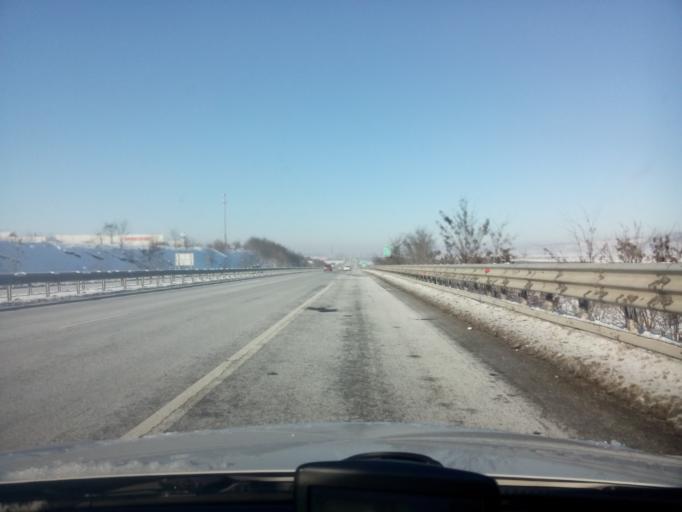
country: RO
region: Arges
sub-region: Oras Stefanesti
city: Golesti
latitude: 44.8170
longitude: 24.9490
